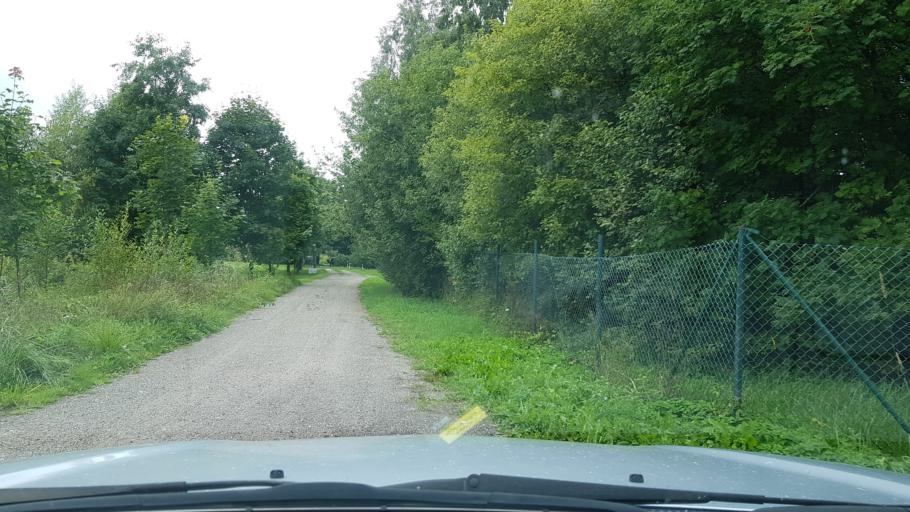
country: EE
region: Harju
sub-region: Joelaehtme vald
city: Loo
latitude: 59.3878
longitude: 24.9403
